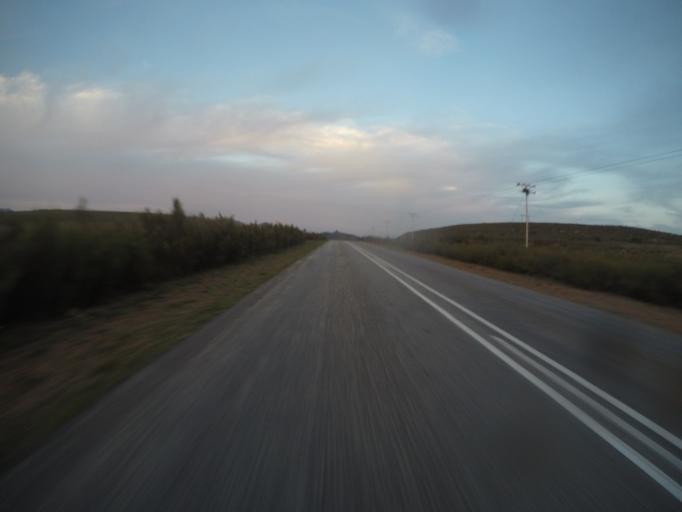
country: ZA
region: Western Cape
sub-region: Eden District Municipality
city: Plettenberg Bay
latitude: -33.7435
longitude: 23.4678
